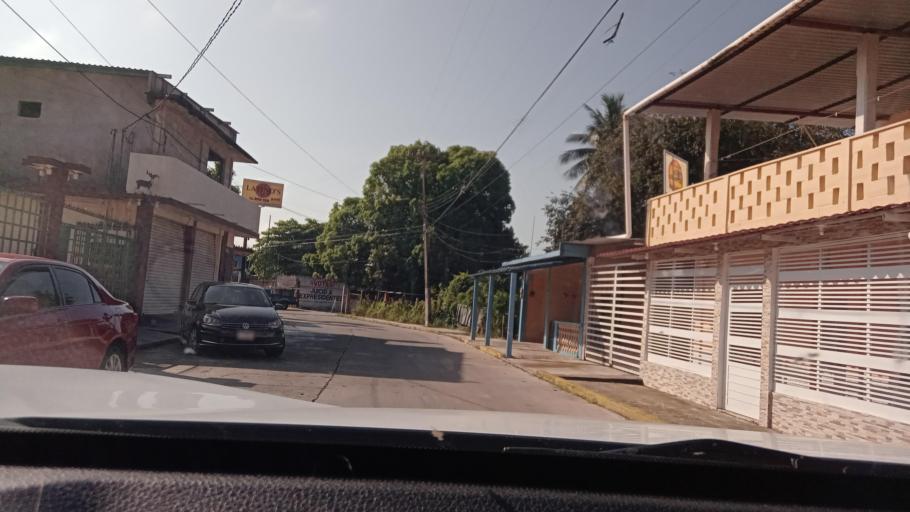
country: MX
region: Veracruz
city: Las Choapas
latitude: 17.9002
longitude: -94.0960
